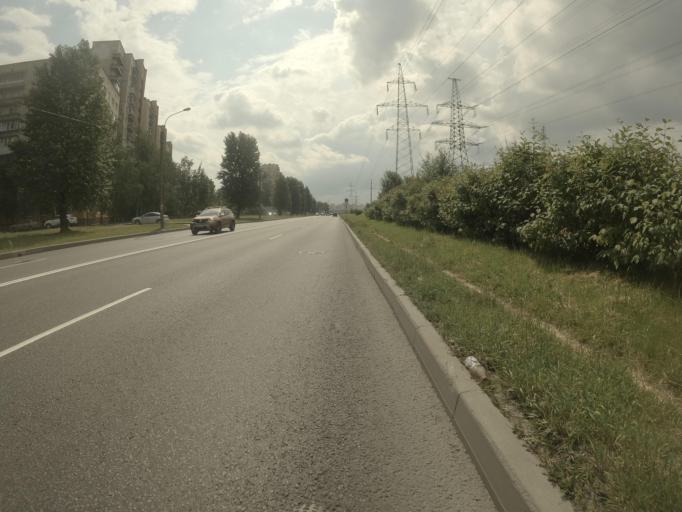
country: RU
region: St.-Petersburg
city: Krasnogvargeisky
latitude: 59.9527
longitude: 30.4605
